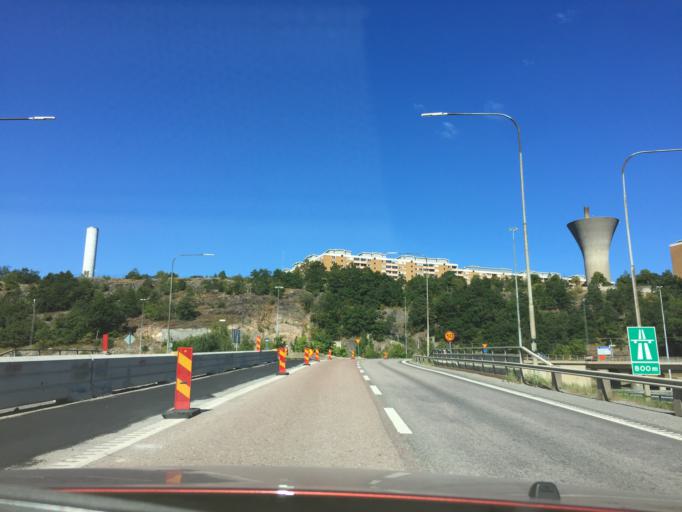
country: SE
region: Stockholm
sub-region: Stockholms Kommun
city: OEstermalm
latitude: 59.3068
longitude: 18.1133
